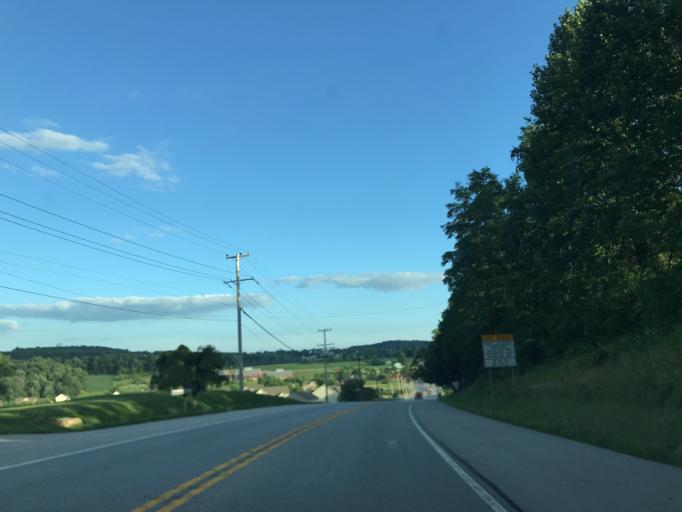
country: US
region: Maryland
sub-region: Carroll County
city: Manchester
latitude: 39.6832
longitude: -76.8920
